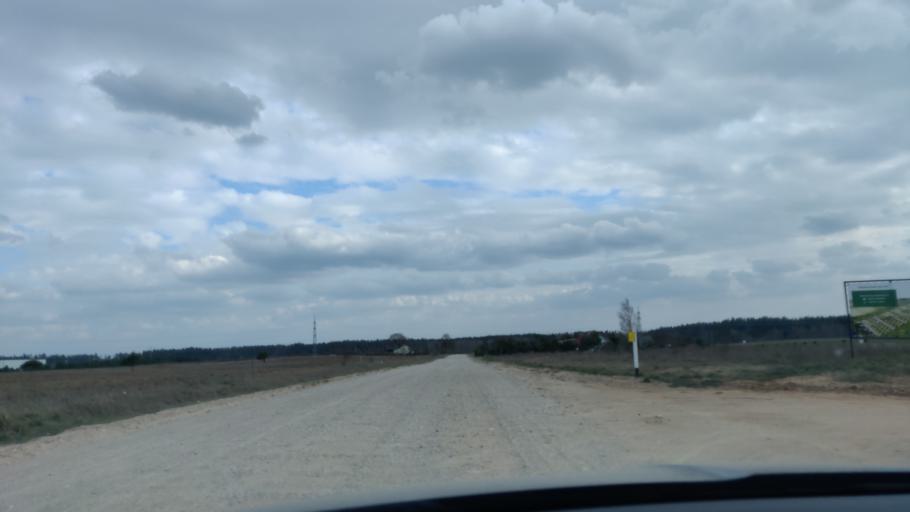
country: LT
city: Lentvaris
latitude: 54.6138
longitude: 25.0692
